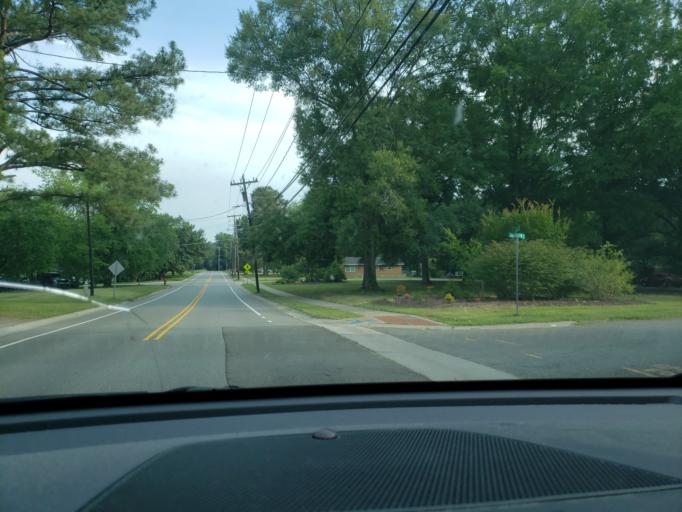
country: US
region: North Carolina
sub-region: Durham County
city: Durham
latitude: 35.9027
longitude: -78.9115
